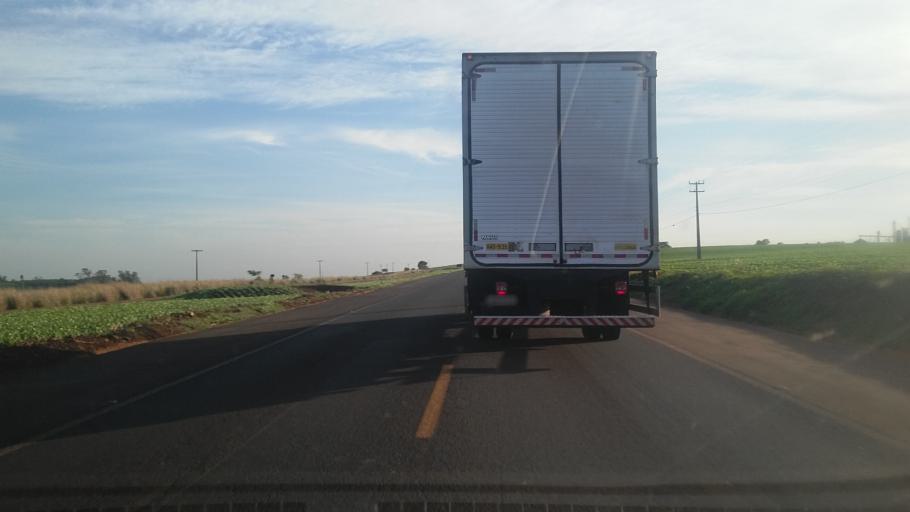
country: BR
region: Parana
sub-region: Bandeirantes
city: Bandeirantes
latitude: -23.1473
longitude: -50.5936
